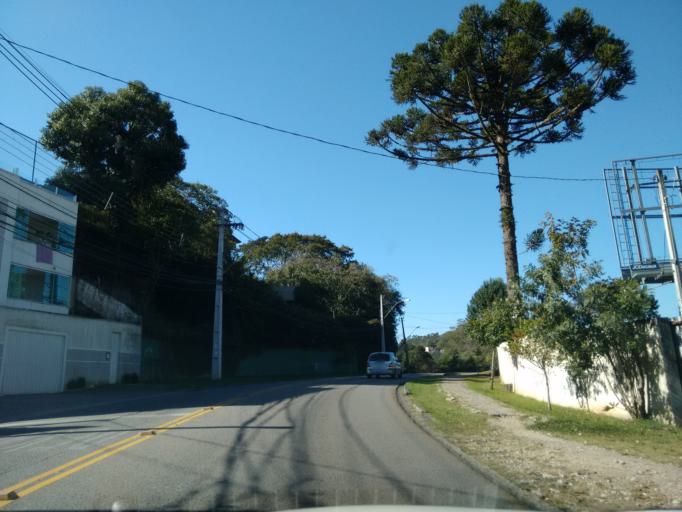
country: BR
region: Parana
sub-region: Curitiba
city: Curitiba
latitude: -25.3943
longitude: -49.2710
